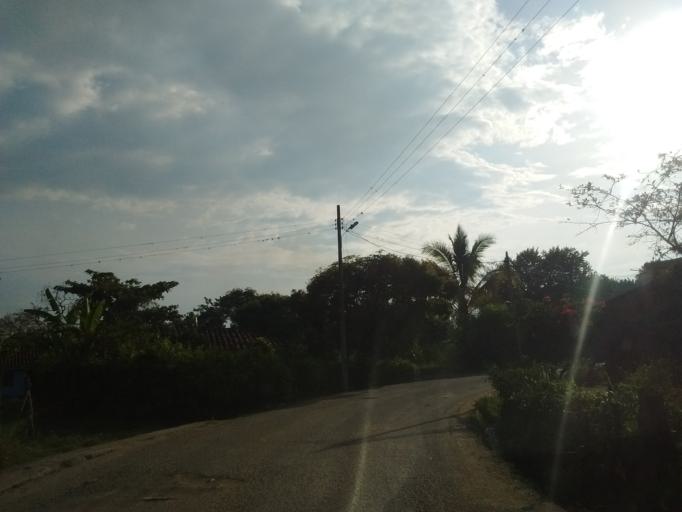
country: CO
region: Cauca
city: Puerto Tejada
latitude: 3.2008
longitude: -76.4416
